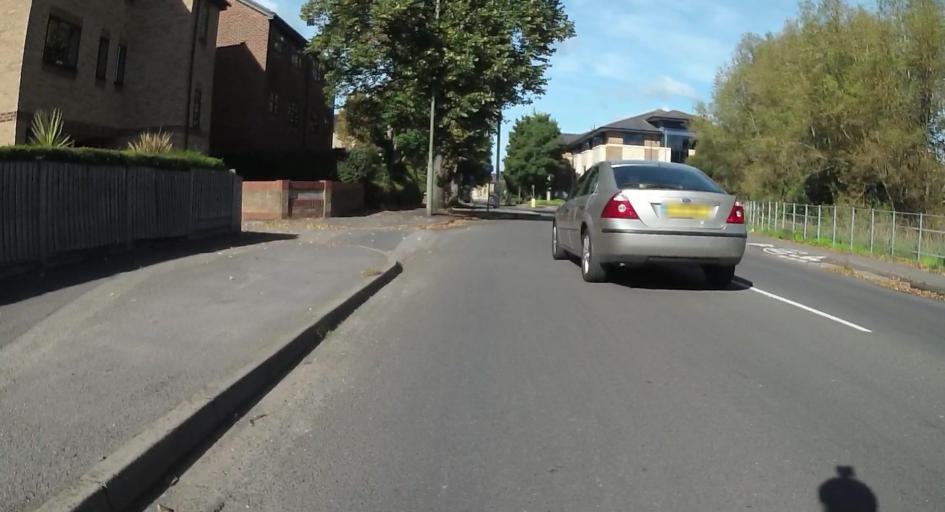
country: GB
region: England
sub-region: Surrey
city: Chertsey
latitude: 51.3867
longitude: -0.5044
